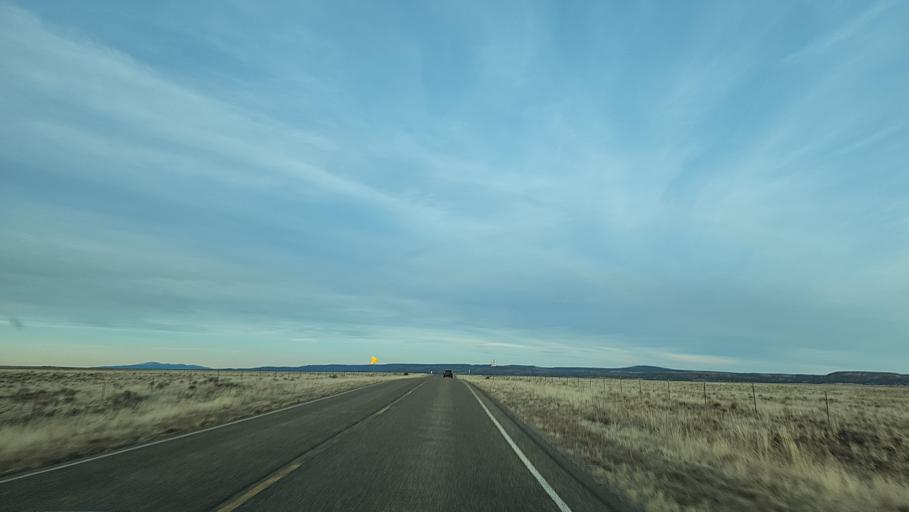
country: US
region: New Mexico
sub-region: Cibola County
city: Grants
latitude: 34.6762
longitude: -108.0845
